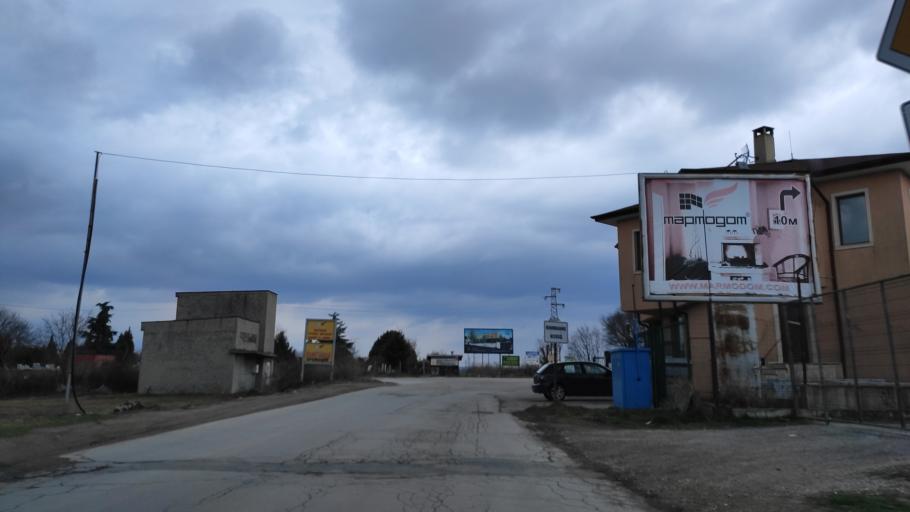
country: BG
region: Varna
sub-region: Obshtina Aksakovo
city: Aksakovo
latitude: 43.2250
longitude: 27.8048
